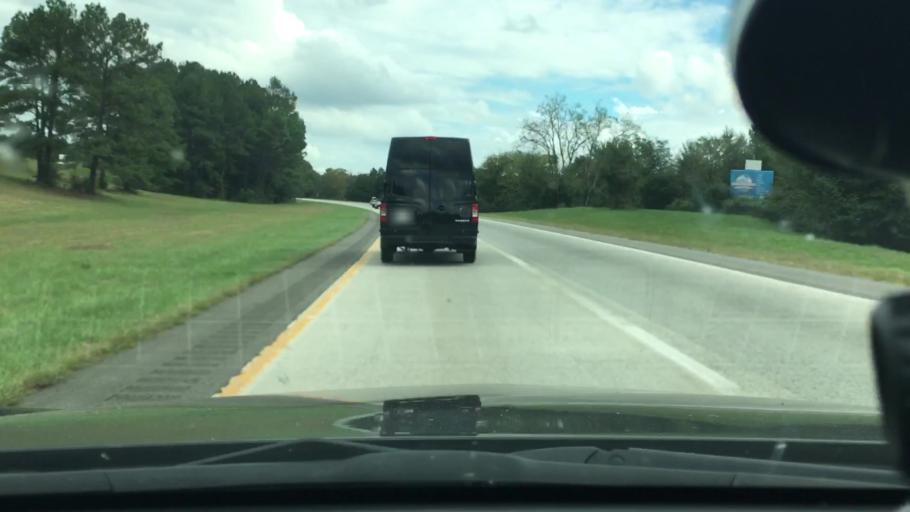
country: US
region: North Carolina
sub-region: Iredell County
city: Statesville
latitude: 35.8488
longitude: -80.7605
